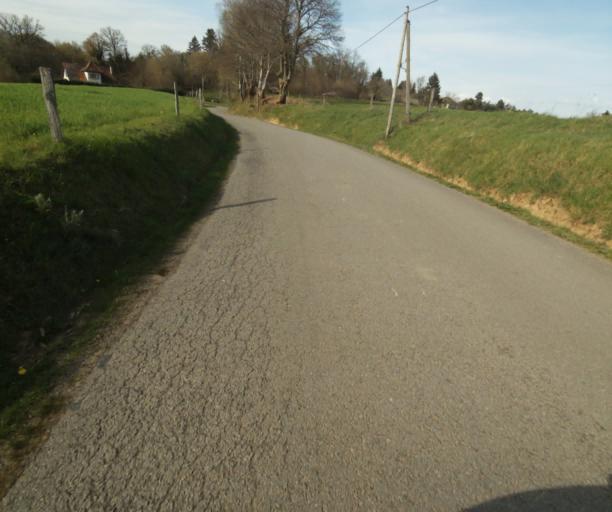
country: FR
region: Limousin
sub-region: Departement de la Correze
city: Naves
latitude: 45.3024
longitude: 1.7388
